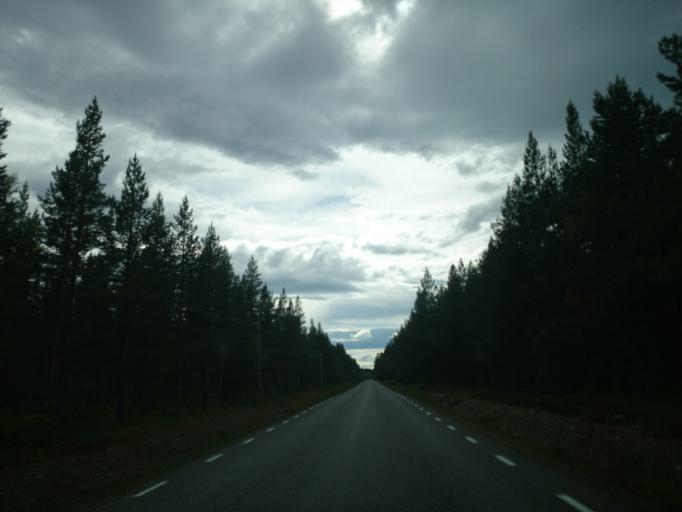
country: SE
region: Jaemtland
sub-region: Are Kommun
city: Are
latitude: 63.1720
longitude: 13.0870
